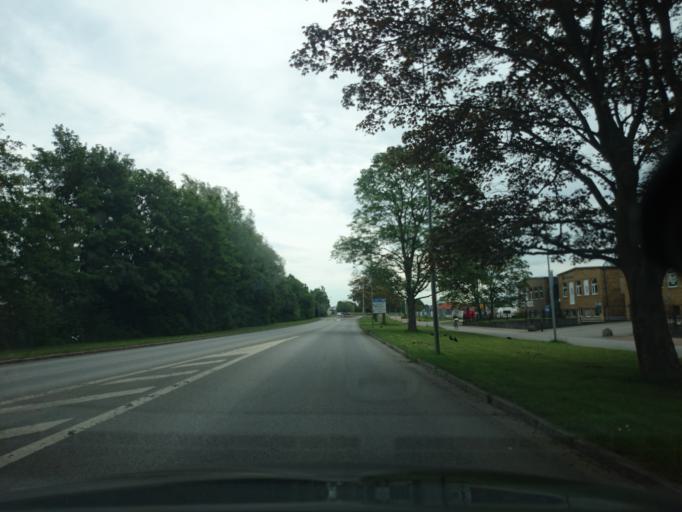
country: SE
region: Skane
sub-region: Landskrona
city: Landskrona
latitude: 55.8852
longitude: 12.8406
